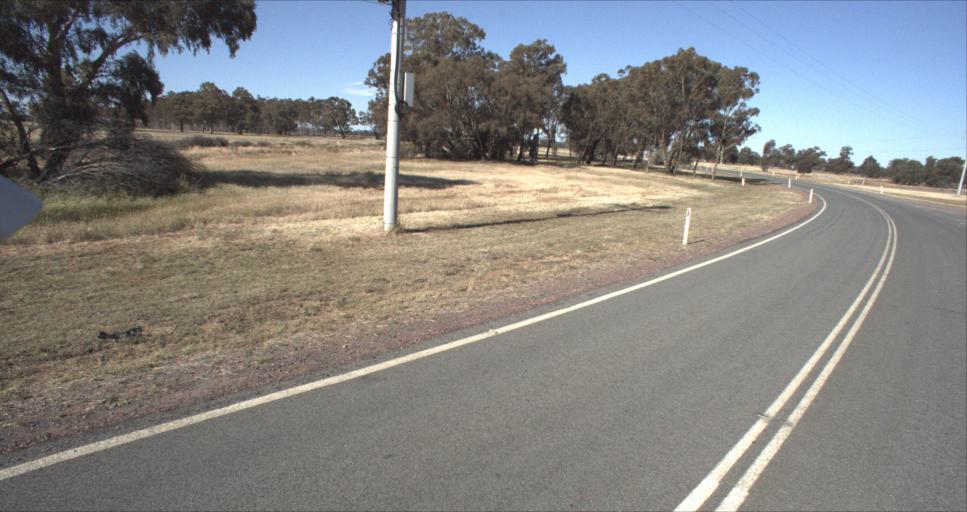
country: AU
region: New South Wales
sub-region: Leeton
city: Leeton
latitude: -34.6258
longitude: 146.3921
